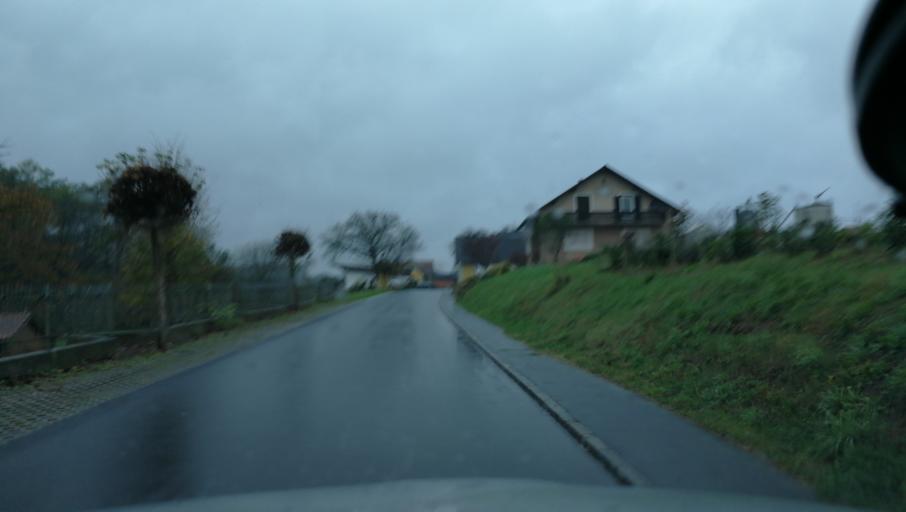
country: AT
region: Styria
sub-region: Politischer Bezirk Leibnitz
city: Strass in Steiermark
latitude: 46.7377
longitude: 15.6460
